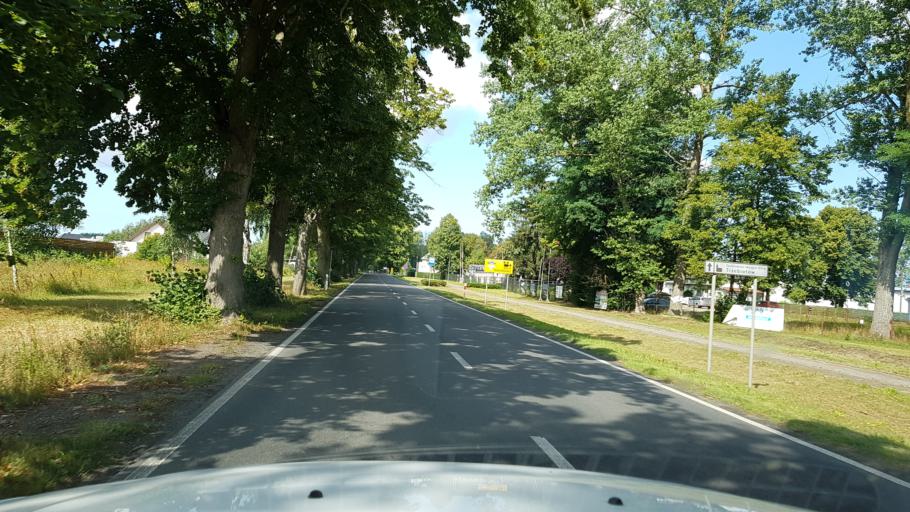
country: PL
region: West Pomeranian Voivodeship
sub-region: Powiat gryficki
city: Trzebiatow
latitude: 54.0624
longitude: 15.2925
